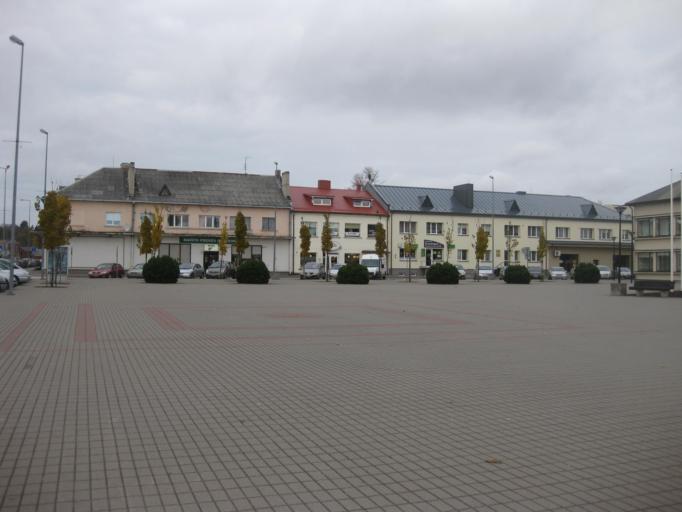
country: LT
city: Prienai
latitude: 54.6351
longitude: 23.9464
